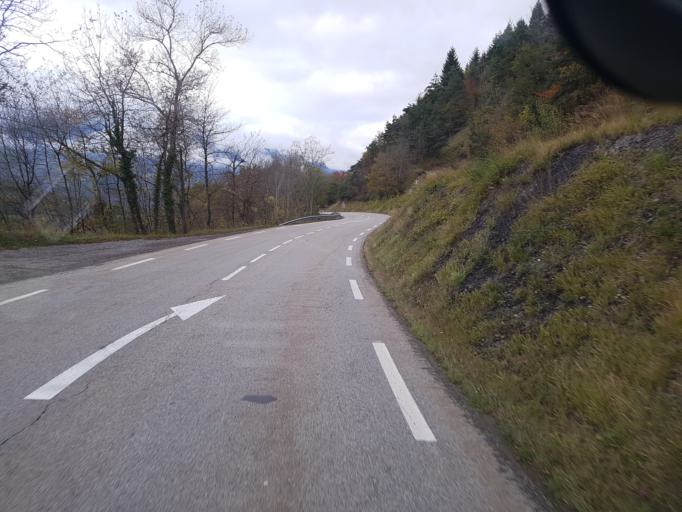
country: FR
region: Rhone-Alpes
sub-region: Departement de l'Isere
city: Le Gua
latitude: 44.9425
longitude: 5.6402
